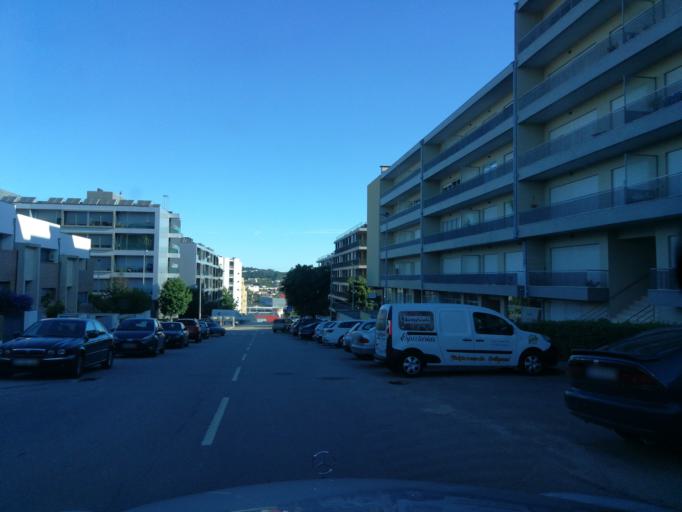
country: PT
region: Braga
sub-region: Braga
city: Braga
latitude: 41.5374
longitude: -8.3969
